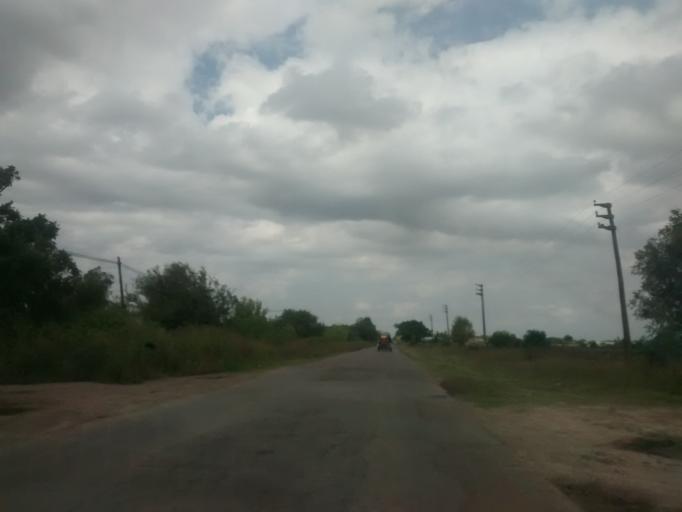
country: AR
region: Buenos Aires
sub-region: Partido de La Plata
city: La Plata
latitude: -34.9854
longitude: -57.9242
